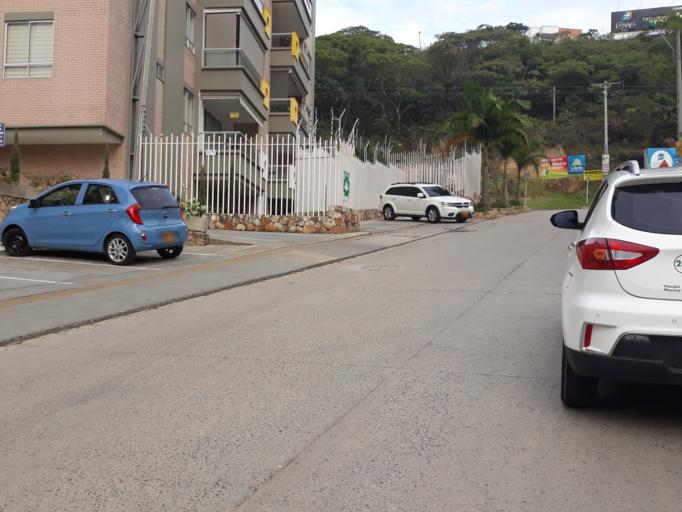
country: CO
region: Valle del Cauca
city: Cali
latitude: 3.4309
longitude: -76.5522
